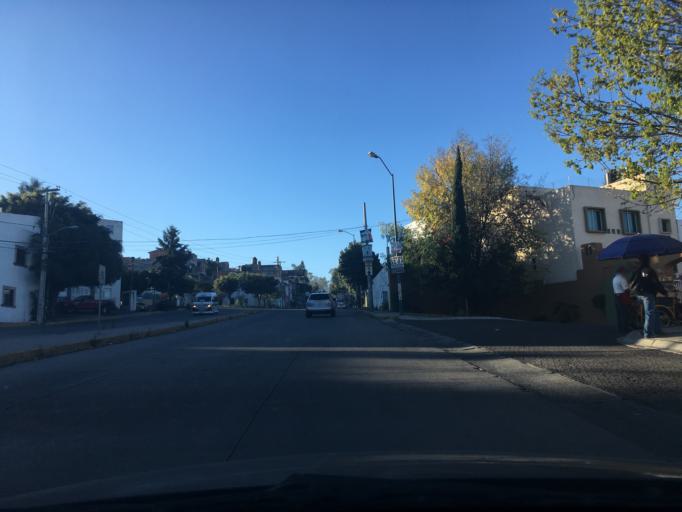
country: MX
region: Michoacan
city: Morelia
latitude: 19.6711
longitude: -101.2010
